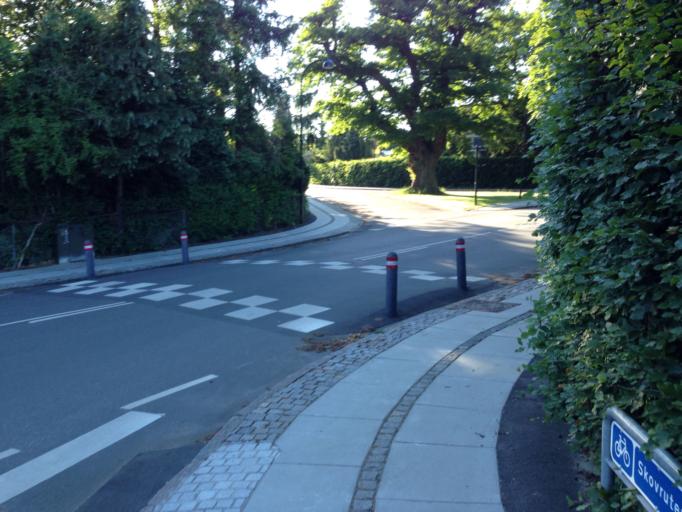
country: DK
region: Capital Region
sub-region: Gentofte Kommune
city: Charlottenlund
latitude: 55.7662
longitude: 12.5737
